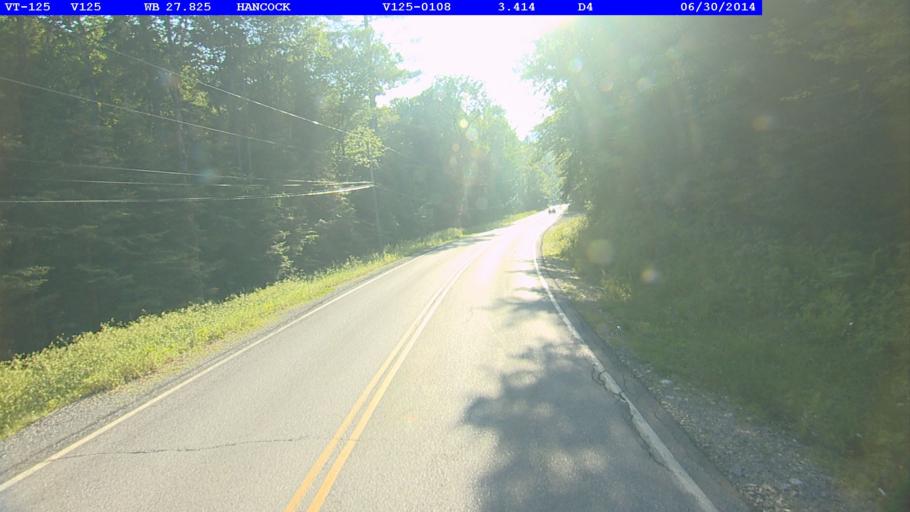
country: US
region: Vermont
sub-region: Rutland County
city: Brandon
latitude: 43.9270
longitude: -72.9146
